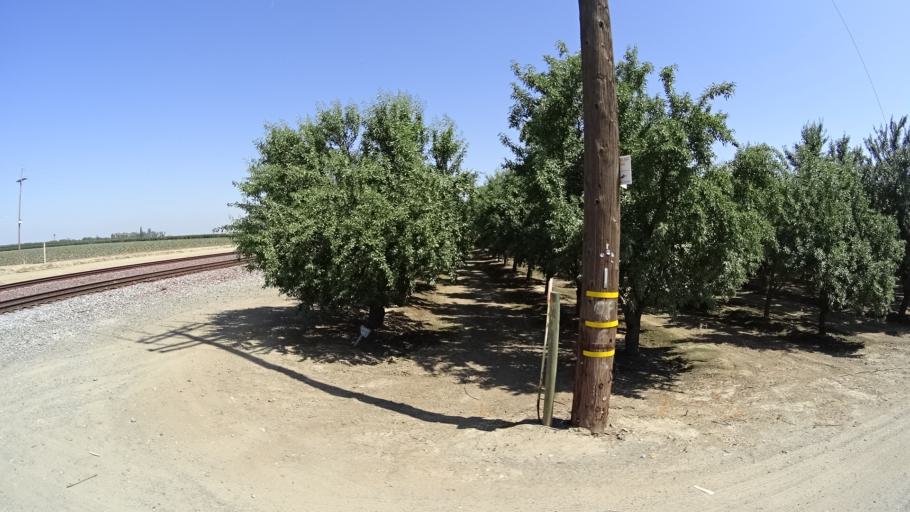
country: US
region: California
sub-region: Kings County
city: Lucerne
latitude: 36.3718
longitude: -119.6638
